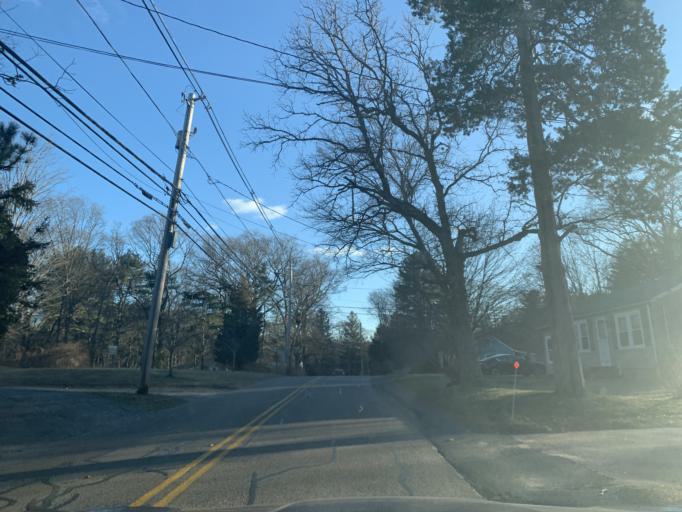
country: US
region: Massachusetts
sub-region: Bristol County
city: Norton
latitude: 41.9413
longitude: -71.2024
